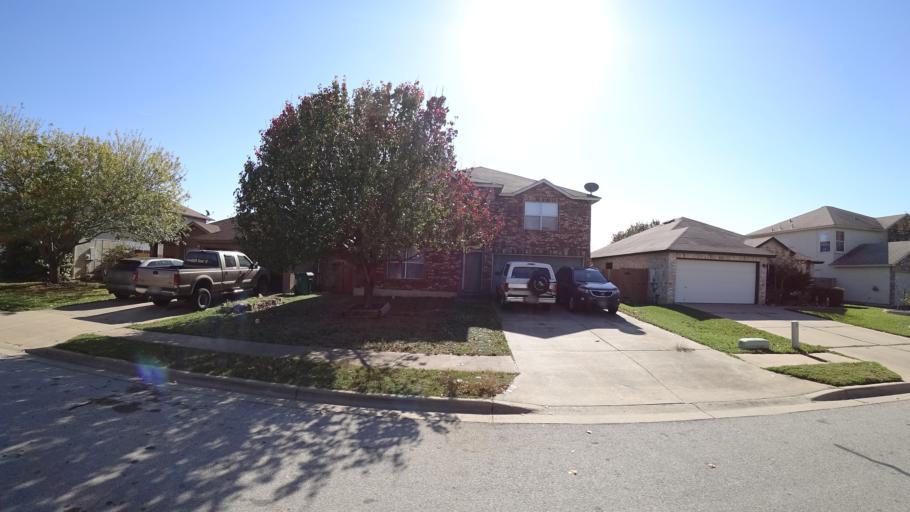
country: US
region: Texas
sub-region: Williamson County
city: Cedar Park
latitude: 30.5373
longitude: -97.8440
